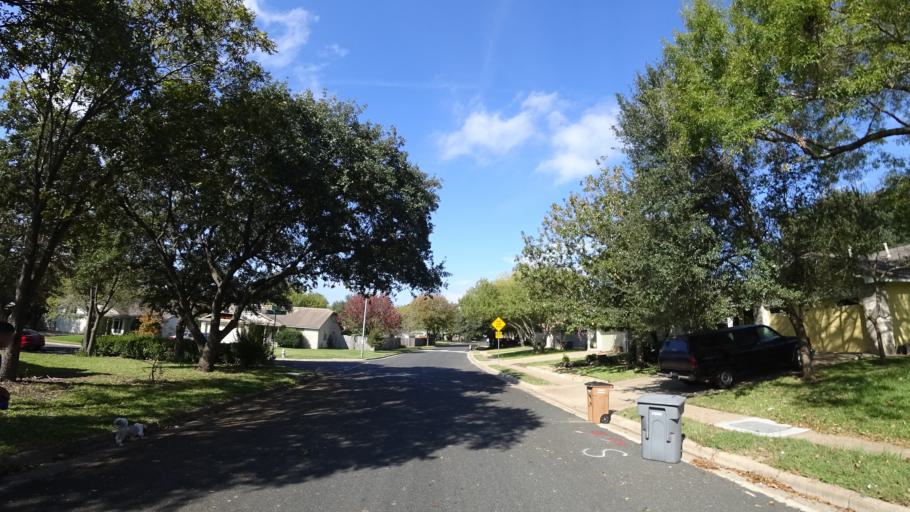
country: US
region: Texas
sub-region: Travis County
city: Shady Hollow
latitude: 30.1979
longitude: -97.8208
